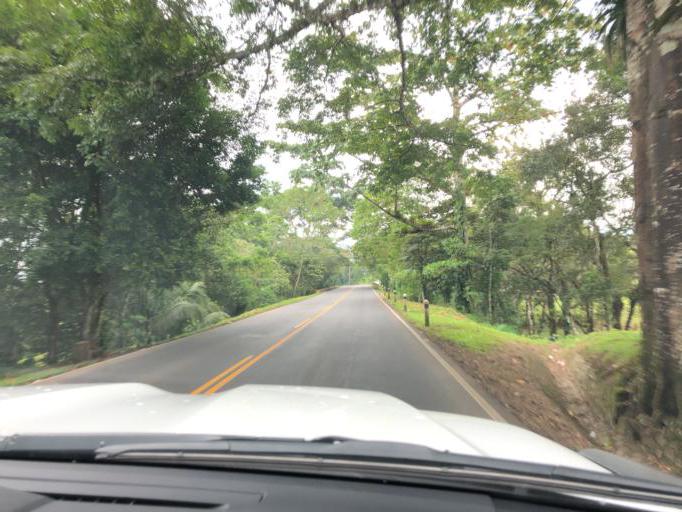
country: NI
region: Chontales
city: Villa Sandino
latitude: 11.9946
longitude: -84.7951
